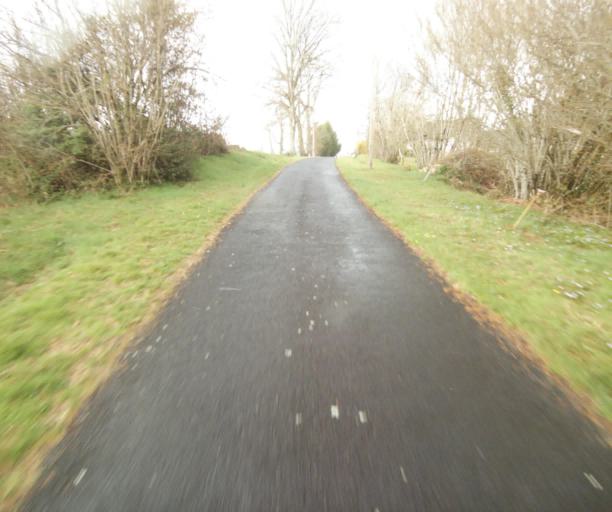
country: FR
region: Limousin
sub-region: Departement de la Correze
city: Saint-Privat
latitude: 45.2566
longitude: 1.9961
